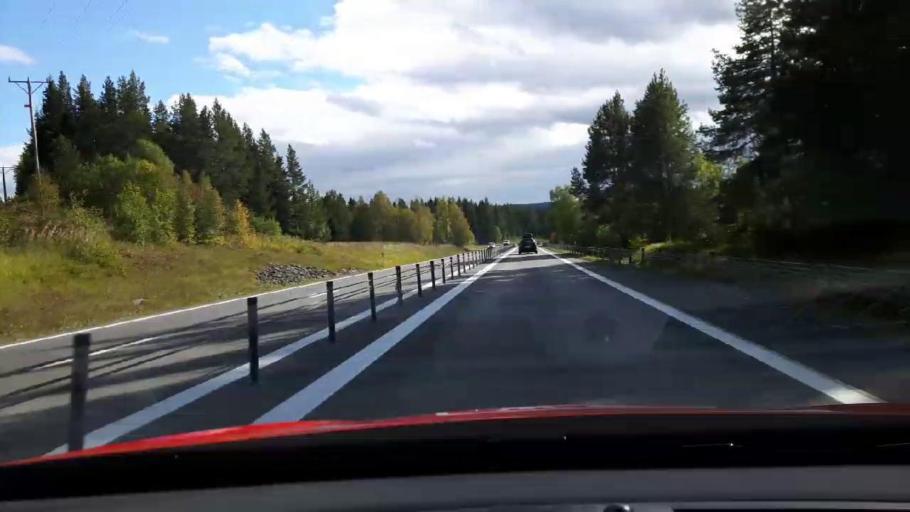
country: SE
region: Jaemtland
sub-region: OEstersunds Kommun
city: Brunflo
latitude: 63.1126
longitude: 14.7972
